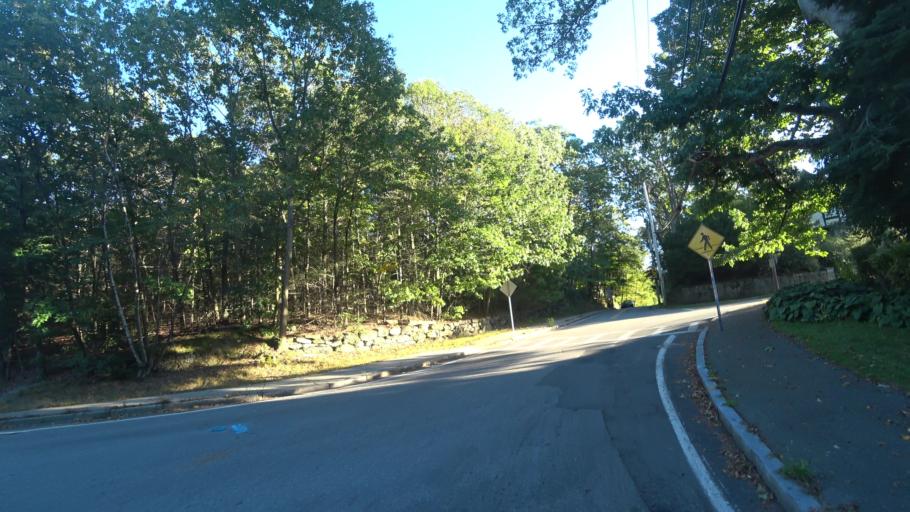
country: US
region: Massachusetts
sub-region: Norfolk County
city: Brookline
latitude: 42.3271
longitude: -71.1316
